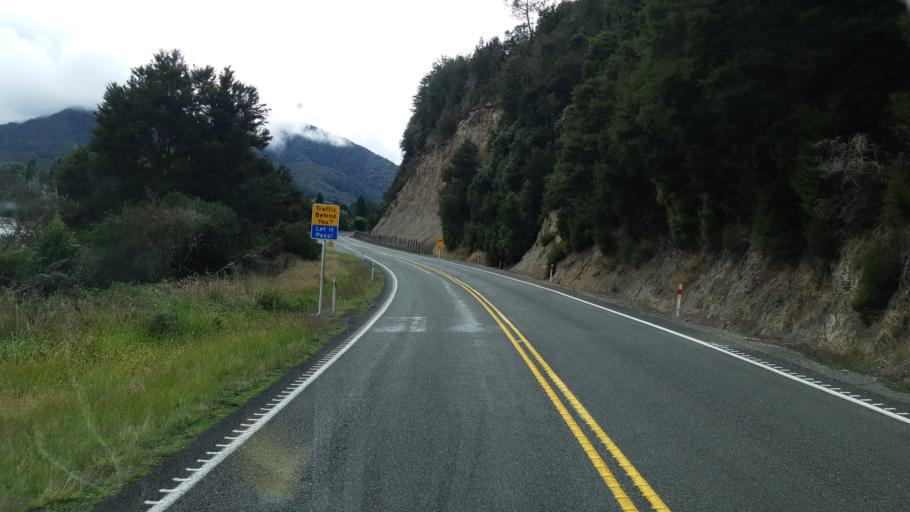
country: NZ
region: West Coast
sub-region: Buller District
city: Westport
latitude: -41.7820
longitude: 172.2680
